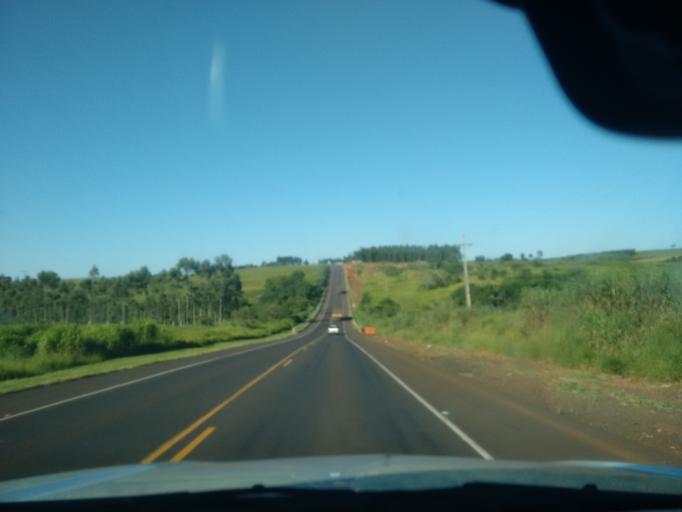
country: PY
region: Canindeyu
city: Salto del Guaira
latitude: -23.9669
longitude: -54.3267
